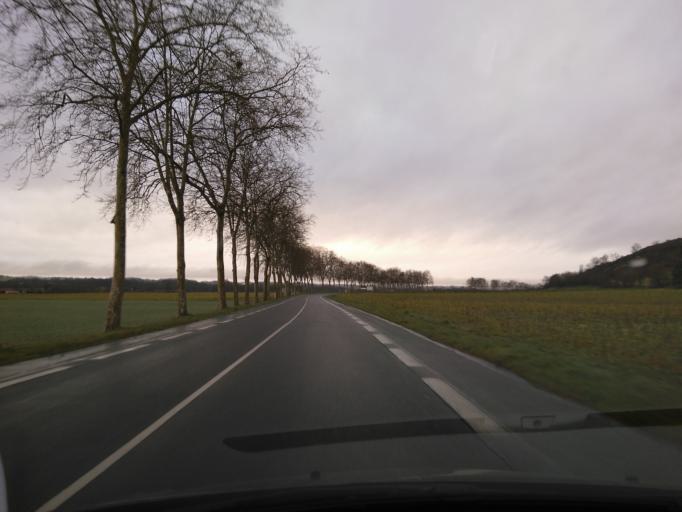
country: FR
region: Midi-Pyrenees
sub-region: Departement de la Haute-Garonne
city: Montesquieu-Volvestre
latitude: 43.2209
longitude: 1.2167
